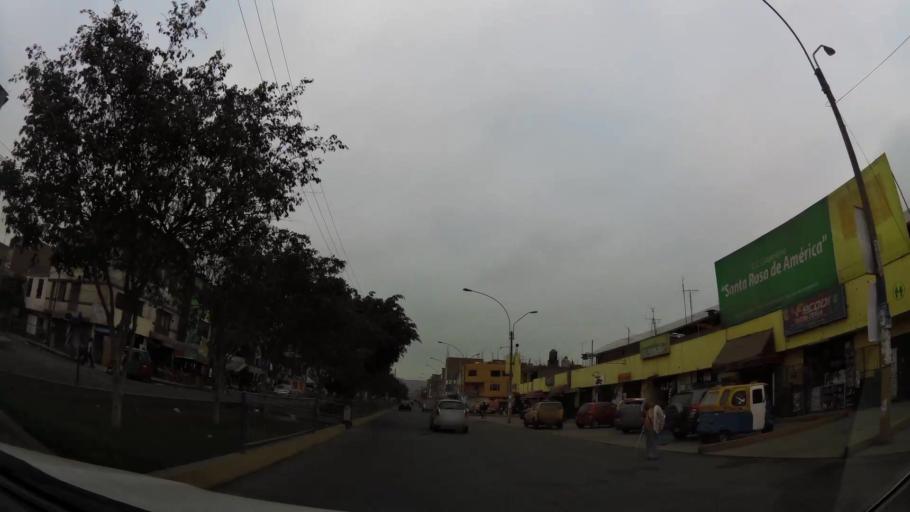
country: PE
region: Lima
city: Lima
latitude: -12.0127
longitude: -77.0087
